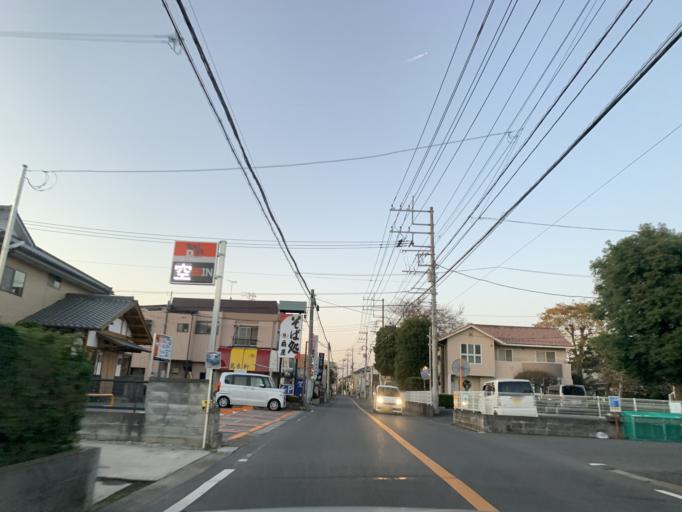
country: JP
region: Chiba
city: Nagareyama
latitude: 35.9021
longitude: 139.9063
